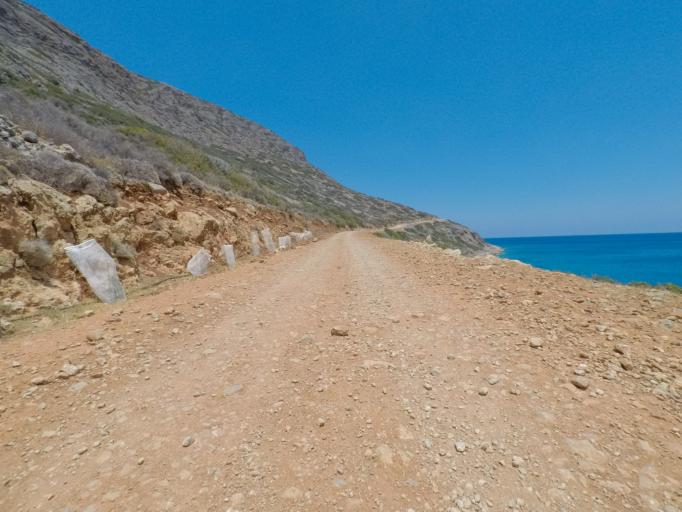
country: GR
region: Crete
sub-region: Nomos Lasithiou
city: Elounda
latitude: 35.3071
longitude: 25.7357
